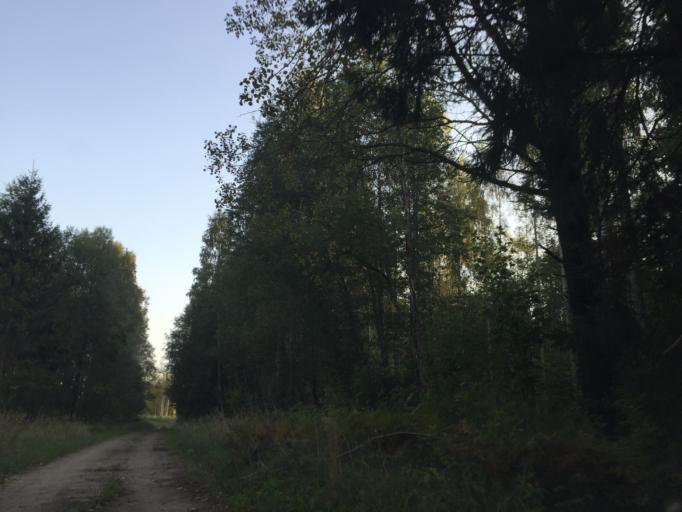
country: LV
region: Lielvarde
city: Lielvarde
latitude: 56.7896
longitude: 24.8337
